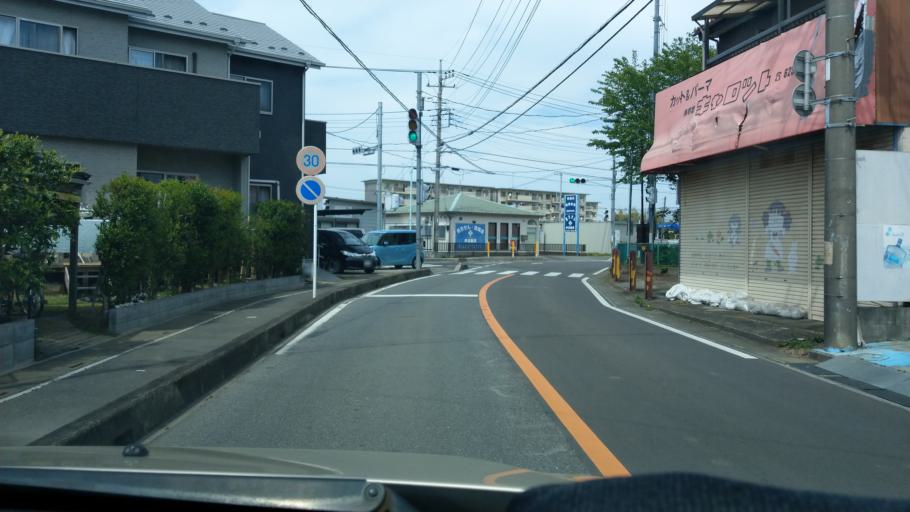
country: JP
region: Saitama
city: Yono
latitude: 35.8858
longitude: 139.5977
